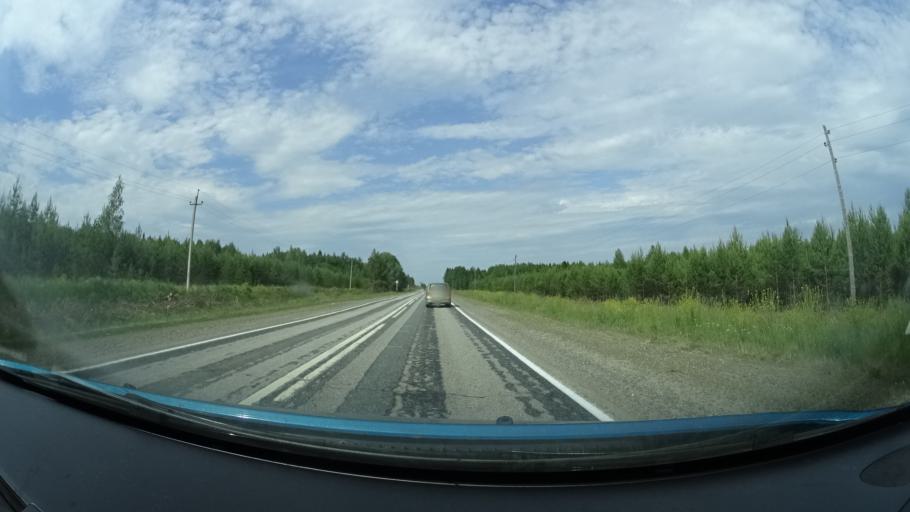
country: RU
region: Perm
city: Osa
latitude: 57.1198
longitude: 55.5231
